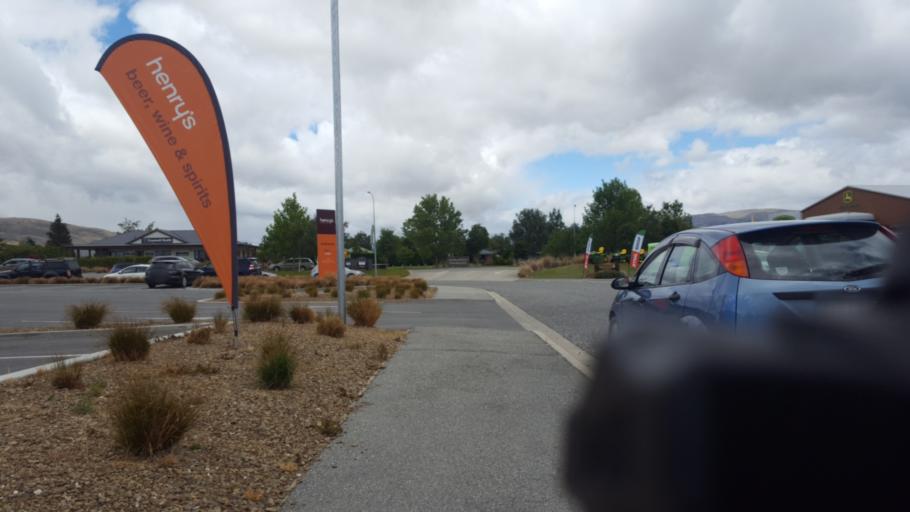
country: NZ
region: Otago
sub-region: Queenstown-Lakes District
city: Wanaka
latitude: -45.0365
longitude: 169.1927
